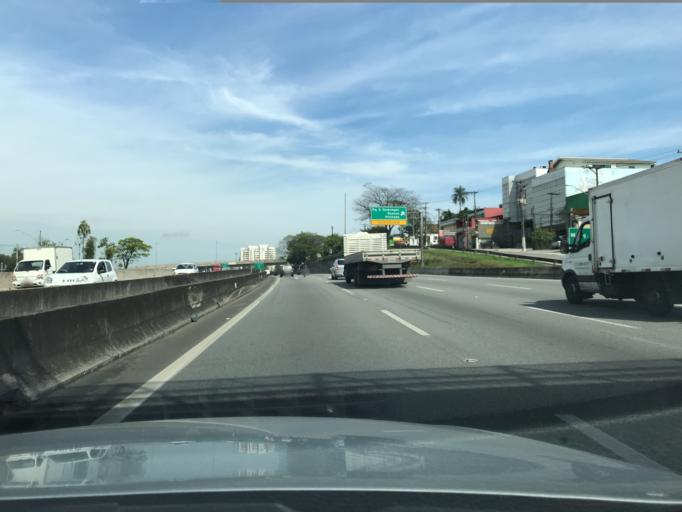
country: BR
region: Sao Paulo
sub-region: Osasco
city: Osasco
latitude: -23.5088
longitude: -46.7317
